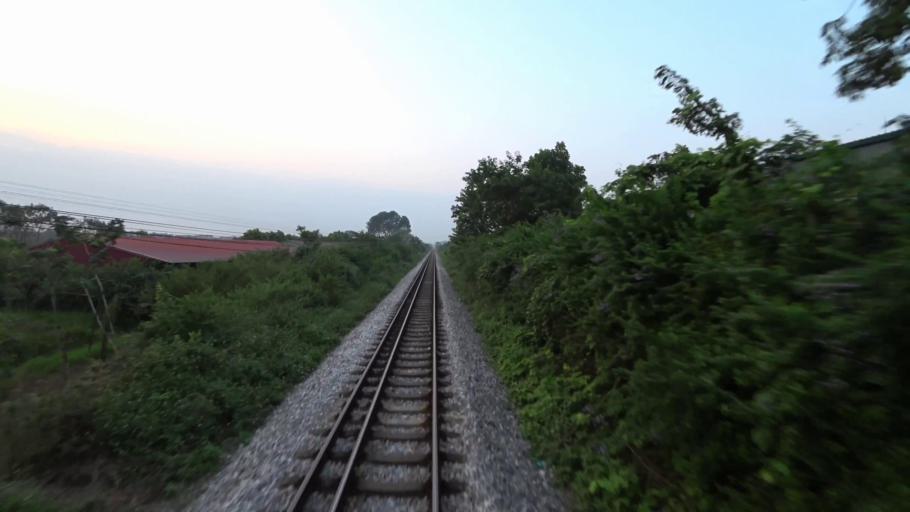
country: VN
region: Ha Noi
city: Dong Anh
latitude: 21.1443
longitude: 105.8621
